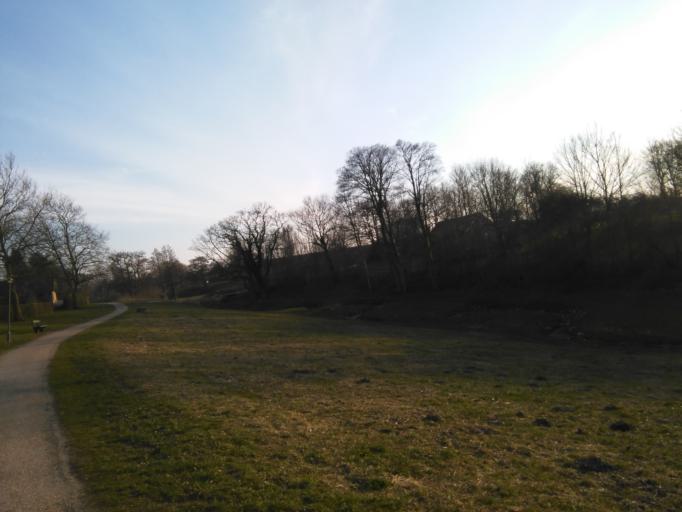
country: DK
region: Central Jutland
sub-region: Arhus Kommune
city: Beder
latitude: 56.0644
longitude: 10.2087
